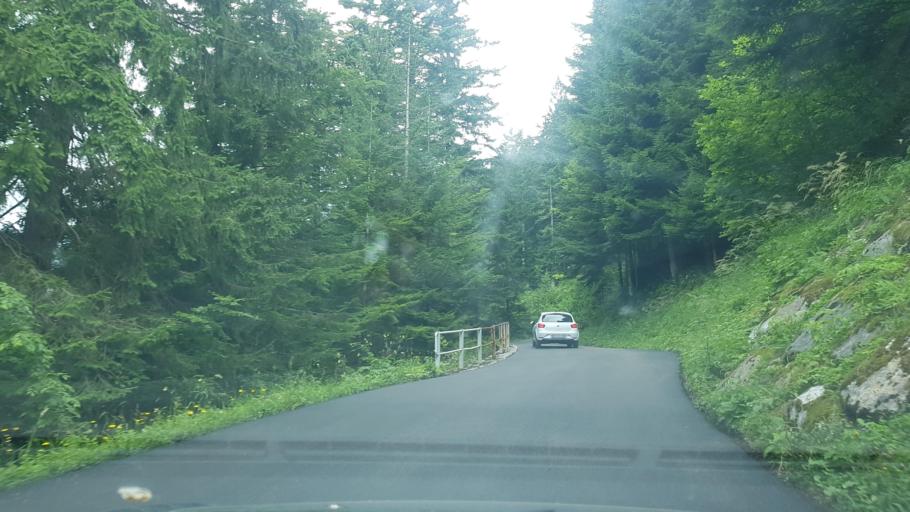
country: IT
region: Friuli Venezia Giulia
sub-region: Provincia di Udine
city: Paularo
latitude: 46.5590
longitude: 13.1251
